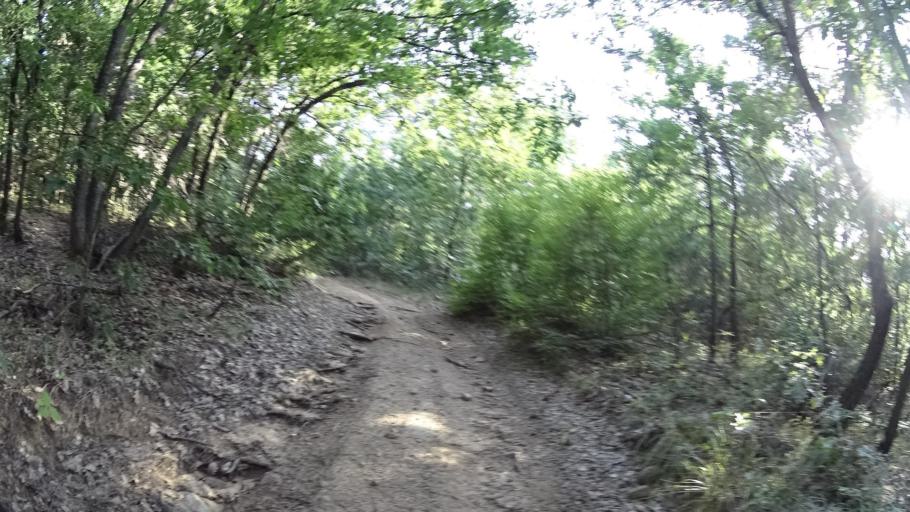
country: BG
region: Plovdiv
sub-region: Obshtina Plovdiv
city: Plovdiv
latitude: 42.0559
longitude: 24.6859
